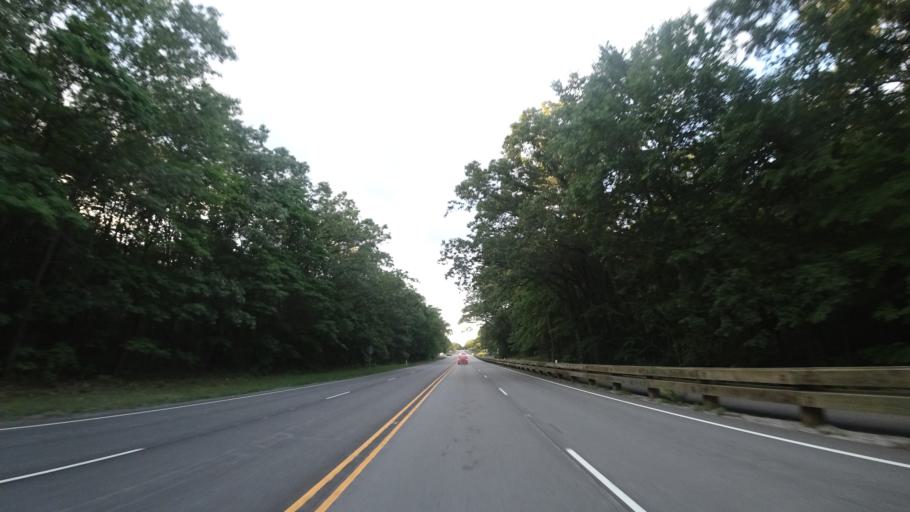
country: US
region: Indiana
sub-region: Porter County
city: Porter
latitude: 41.6402
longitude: -87.0625
